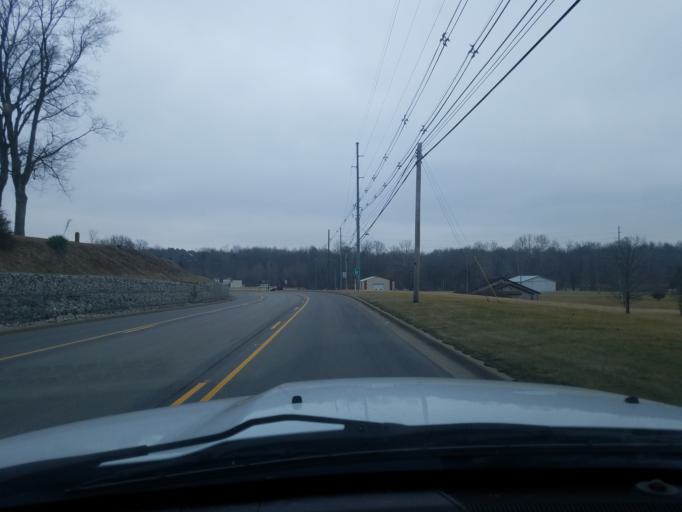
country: US
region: Indiana
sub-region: Perry County
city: Tell City
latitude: 37.9628
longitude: -86.7507
